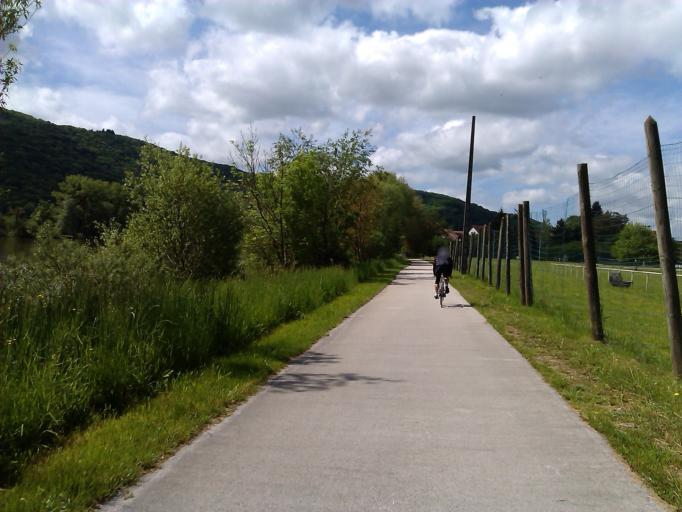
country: FR
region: Franche-Comte
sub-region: Departement du Doubs
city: Novillars
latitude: 47.2763
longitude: 6.1196
